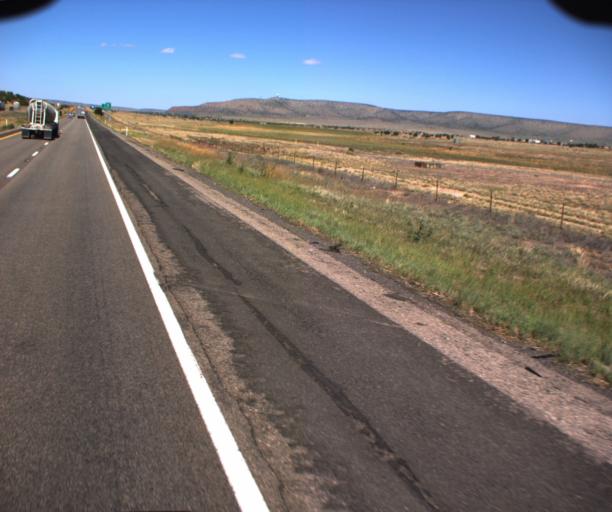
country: US
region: Arizona
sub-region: Mohave County
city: Peach Springs
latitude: 35.3170
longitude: -112.8751
